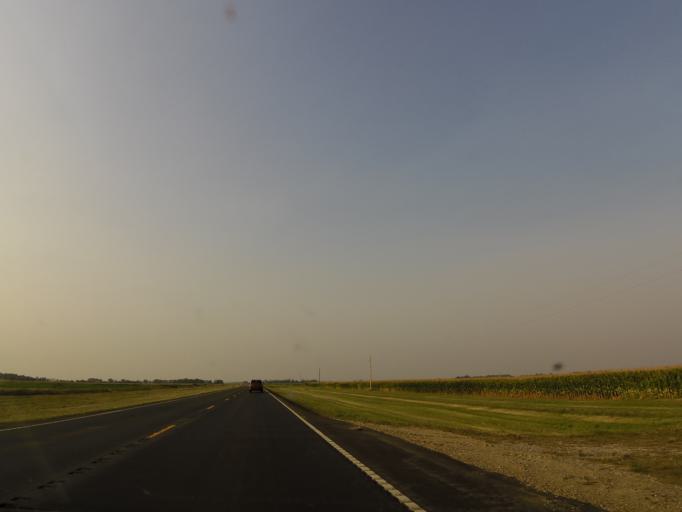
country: US
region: North Dakota
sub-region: Traill County
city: Mayville
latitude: 47.4443
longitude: -97.3259
